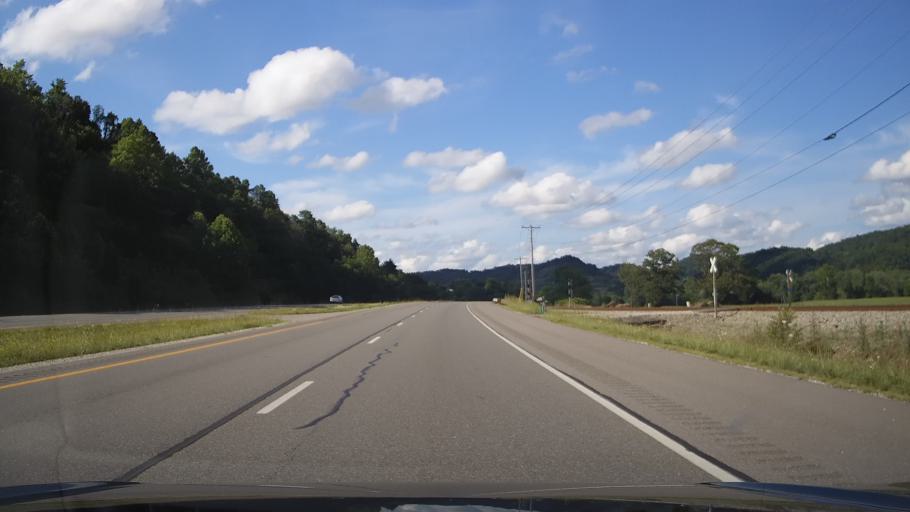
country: US
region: Kentucky
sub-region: Lawrence County
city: Louisa
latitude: 38.1998
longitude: -82.6041
